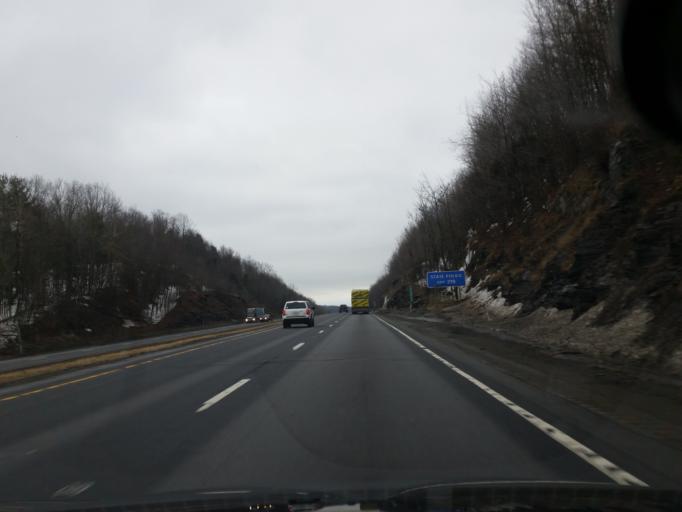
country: US
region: Pennsylvania
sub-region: Susquehanna County
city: Susquehanna
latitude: 41.8438
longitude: -75.6827
